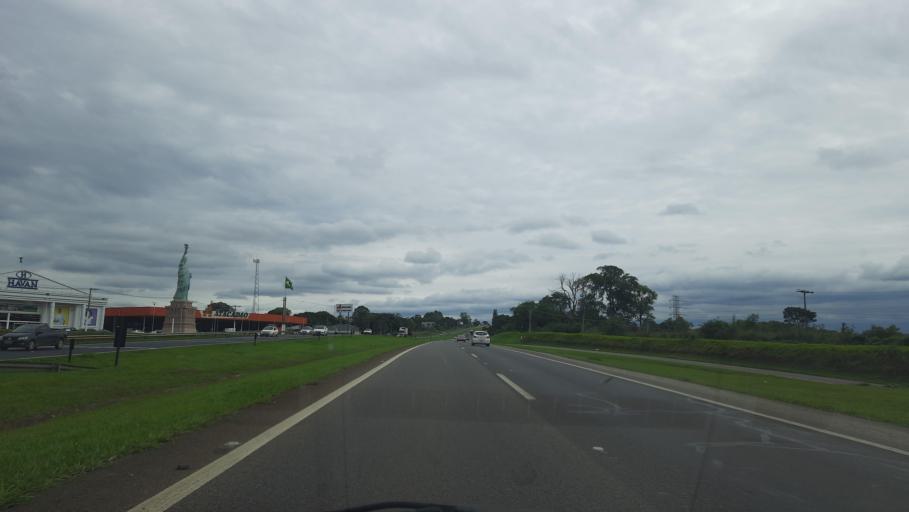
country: BR
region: Sao Paulo
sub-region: Mogi-Mirim
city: Mogi Mirim
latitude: -22.3991
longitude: -46.9732
